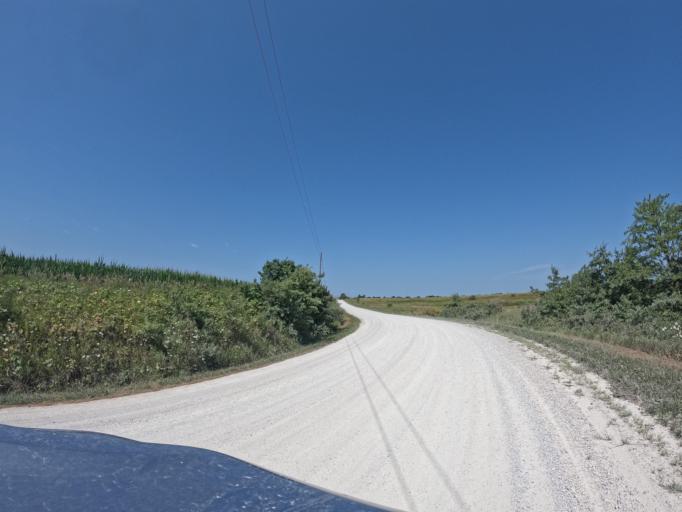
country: US
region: Iowa
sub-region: Henry County
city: Mount Pleasant
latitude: 40.8892
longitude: -91.5752
